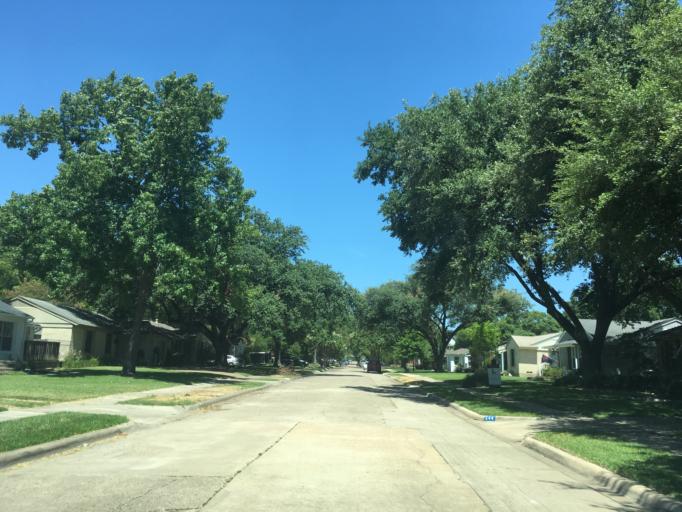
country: US
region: Texas
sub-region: Dallas County
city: Highland Park
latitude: 32.8516
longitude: -96.7089
